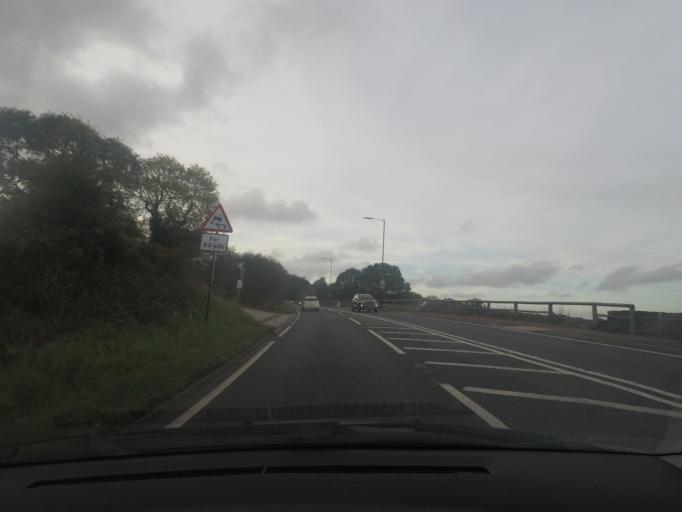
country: GB
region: England
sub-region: Sheffield
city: Chapletown
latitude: 53.4568
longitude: -1.4960
